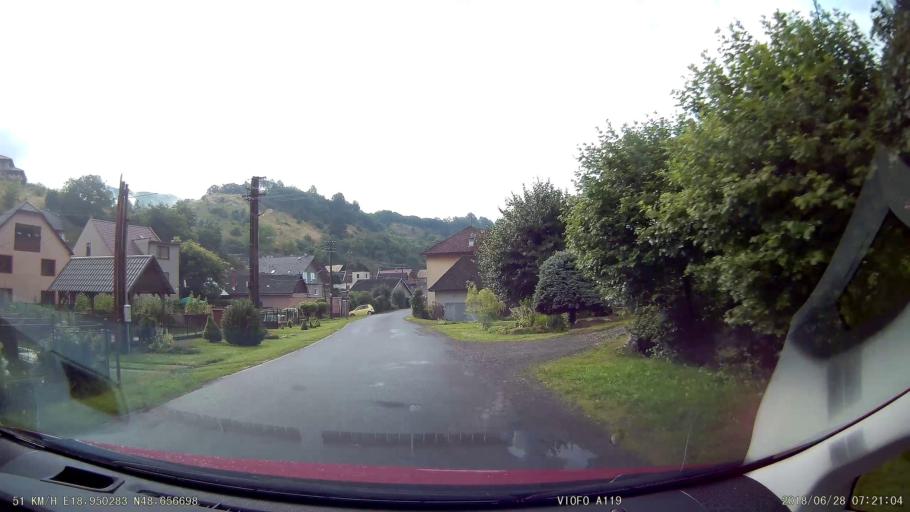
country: SK
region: Banskobystricky
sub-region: Okres Ziar nad Hronom
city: Kremnica
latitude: 48.6565
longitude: 18.9508
